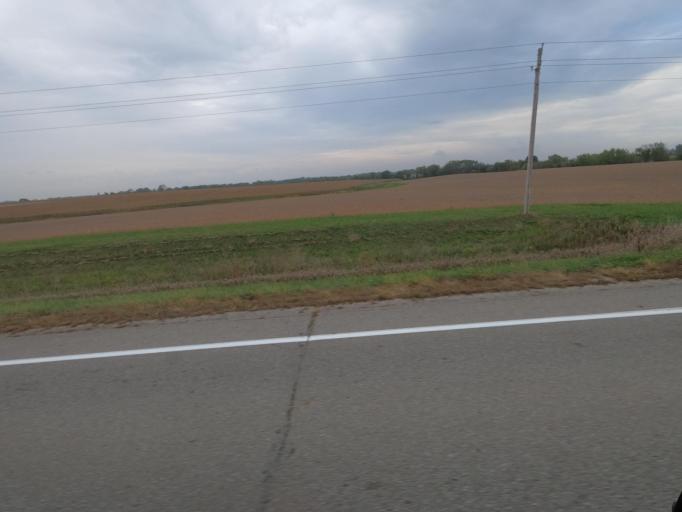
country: US
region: Iowa
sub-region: Henry County
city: Mount Pleasant
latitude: 40.8135
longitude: -91.7257
